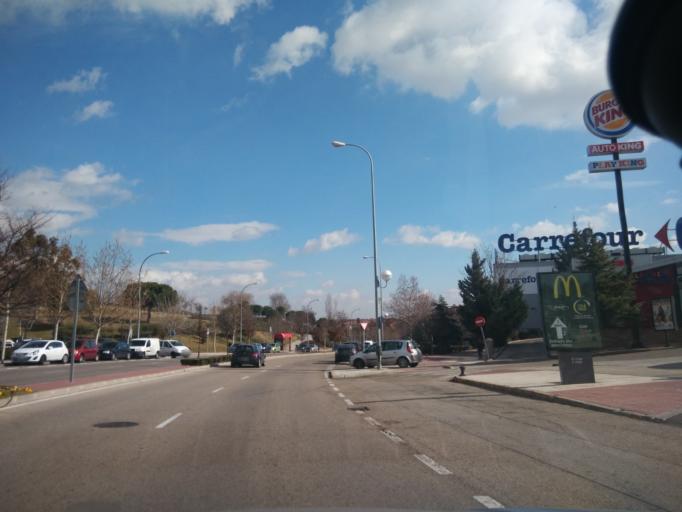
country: ES
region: Madrid
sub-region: Provincia de Madrid
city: Alcobendas
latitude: 40.5486
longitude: -3.6620
